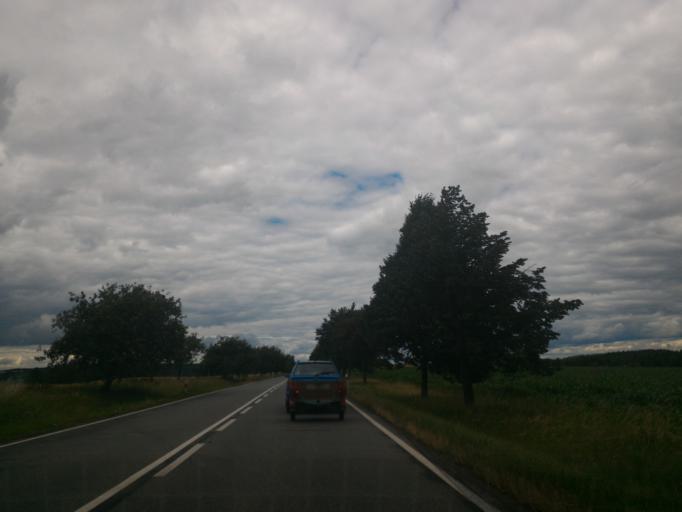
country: CZ
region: Vysocina
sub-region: Okres Pelhrimov
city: Pelhrimov
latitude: 49.4499
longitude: 15.1928
